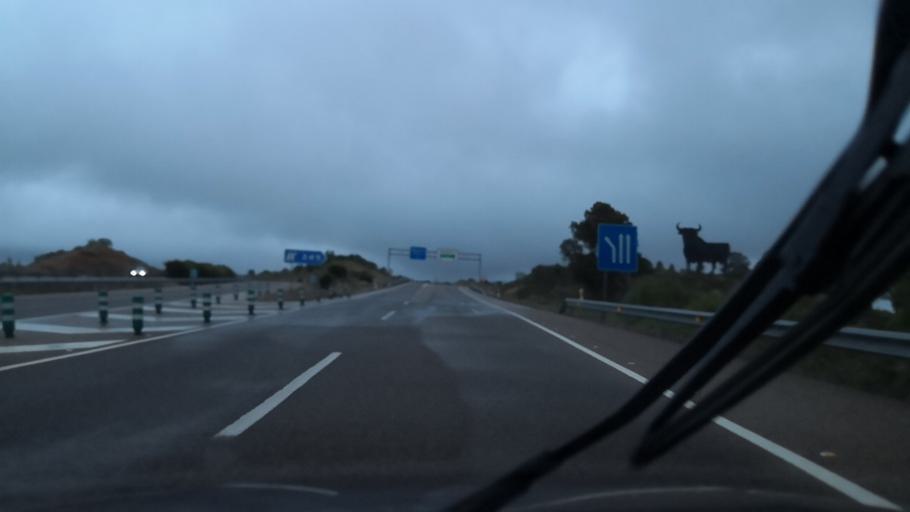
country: ES
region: Extremadura
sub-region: Provincia de Badajoz
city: Calamonte
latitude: 38.9078
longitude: -6.3836
